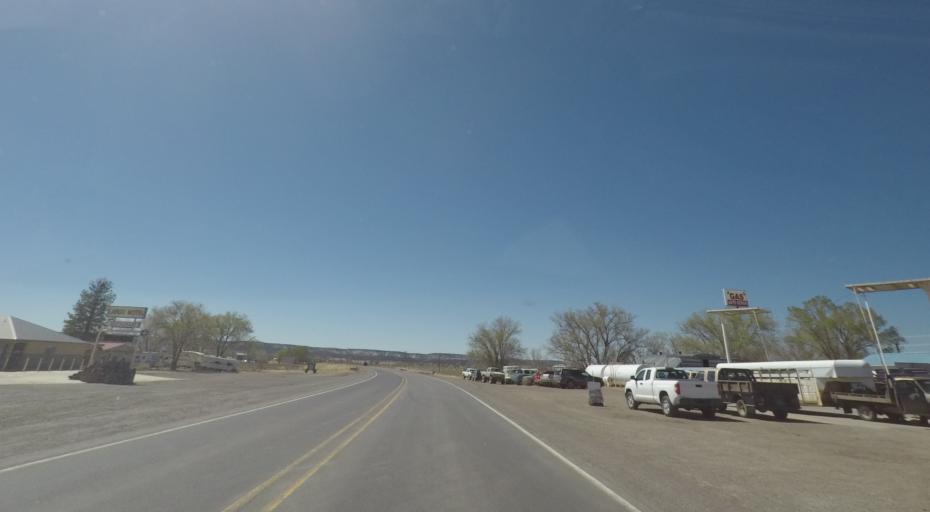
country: US
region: New Mexico
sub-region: Catron County
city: Reserve
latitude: 34.3439
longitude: -108.4997
